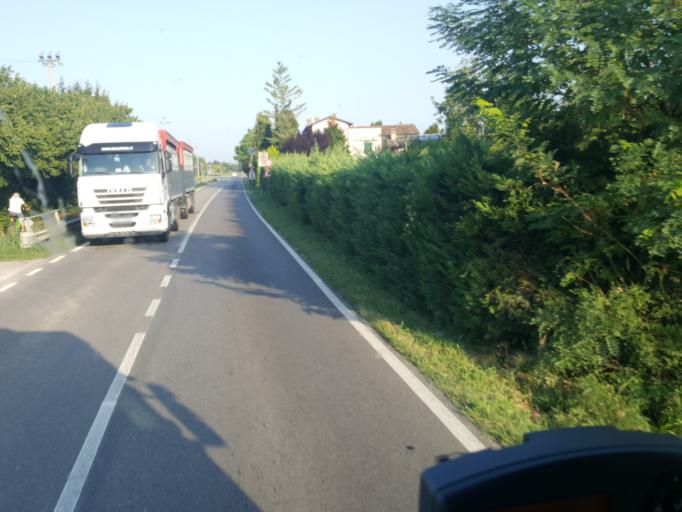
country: IT
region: Emilia-Romagna
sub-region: Provincia di Modena
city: Spilamberto
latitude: 44.5356
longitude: 11.0044
